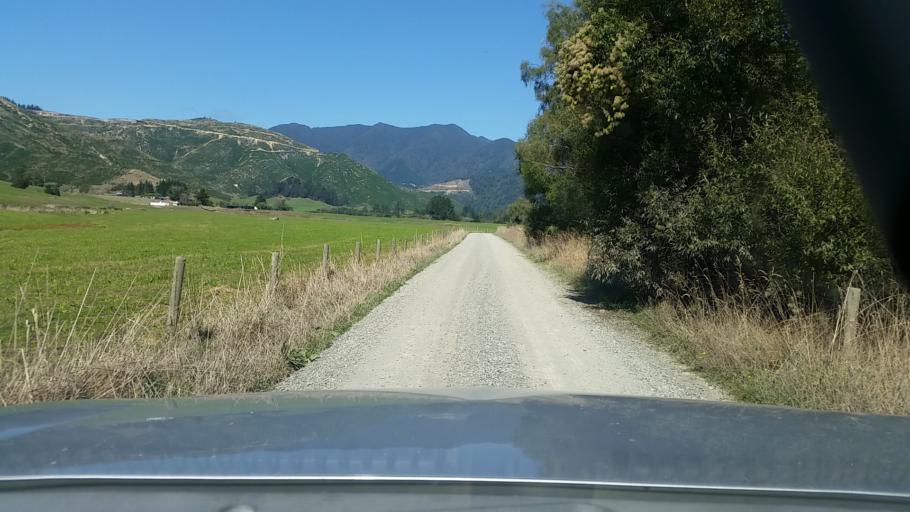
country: NZ
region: Nelson
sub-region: Nelson City
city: Nelson
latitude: -41.2649
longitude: 173.5763
